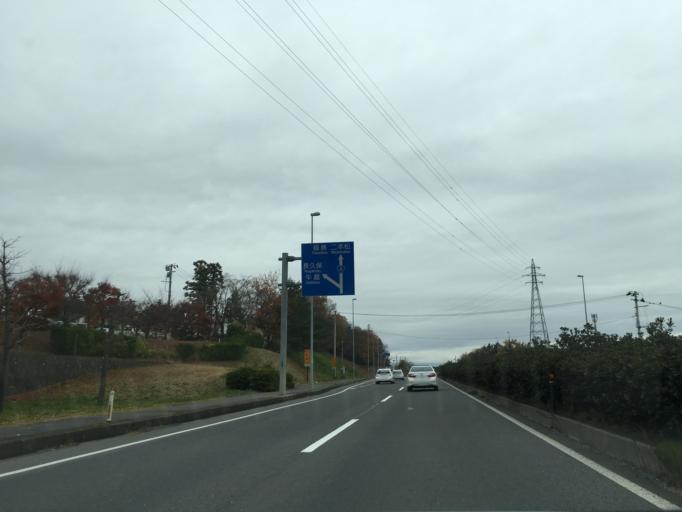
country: JP
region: Fukushima
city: Koriyama
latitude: 37.3540
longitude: 140.3544
